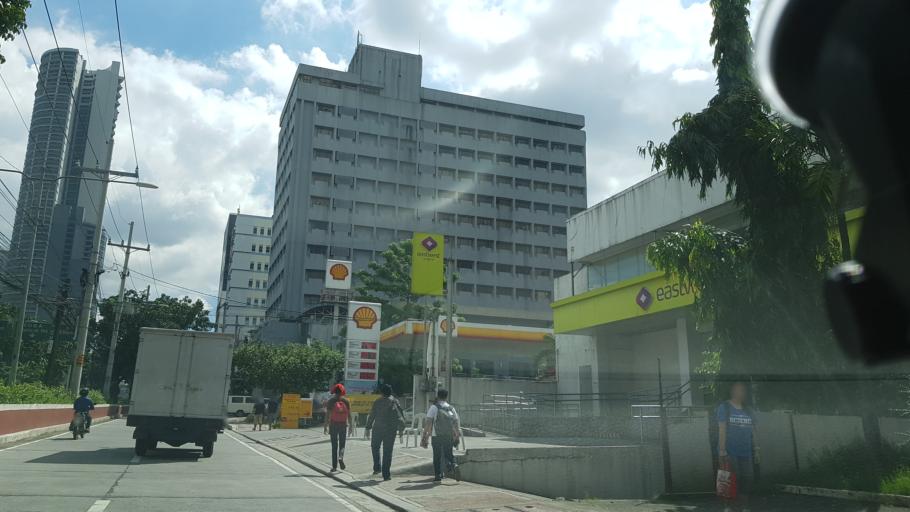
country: PH
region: Calabarzon
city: Del Monte
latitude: 14.6412
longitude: 121.0331
